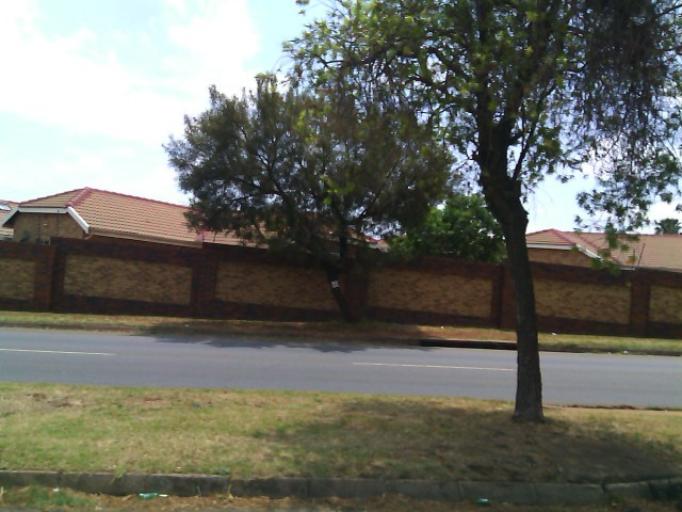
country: ZA
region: Gauteng
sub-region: City of Tshwane Metropolitan Municipality
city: Centurion
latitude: -25.8396
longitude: 28.1889
